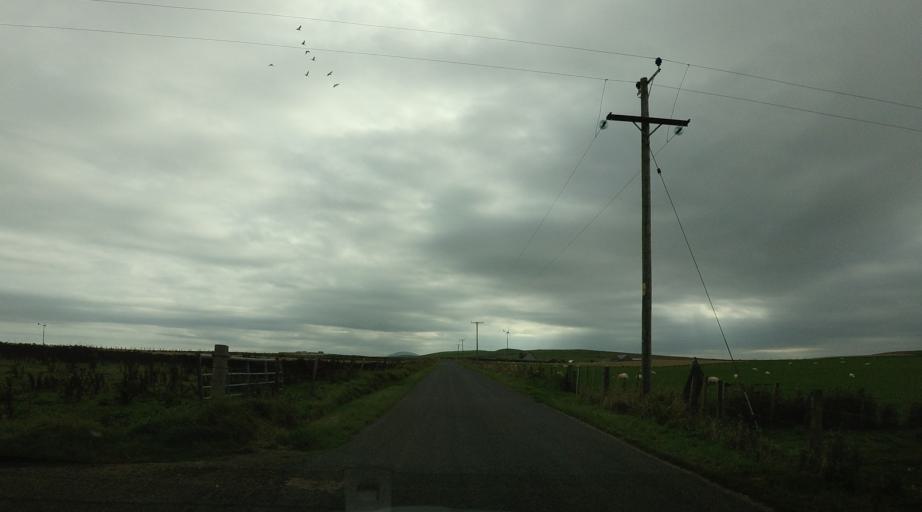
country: GB
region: Scotland
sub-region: Orkney Islands
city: Stromness
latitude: 59.0367
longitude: -3.3118
